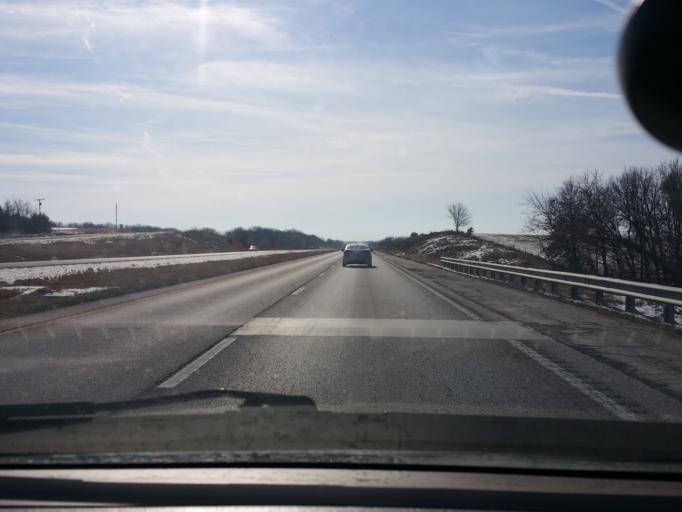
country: US
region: Missouri
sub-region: Clinton County
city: Cameron
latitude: 39.7116
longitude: -94.2249
